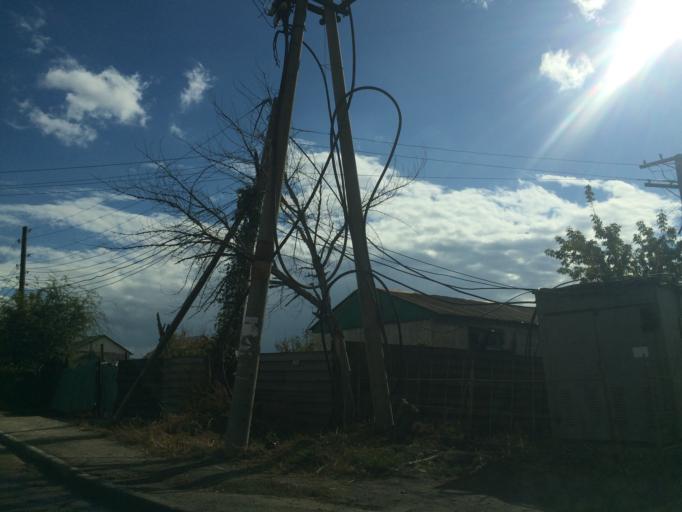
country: KZ
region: Astana Qalasy
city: Astana
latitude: 51.1873
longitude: 71.3834
